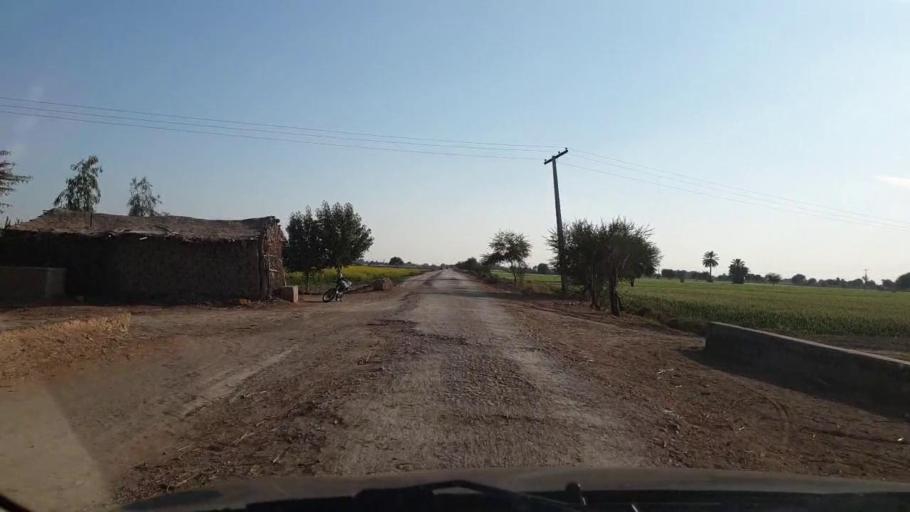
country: PK
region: Sindh
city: Jhol
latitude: 25.9616
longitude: 68.8615
